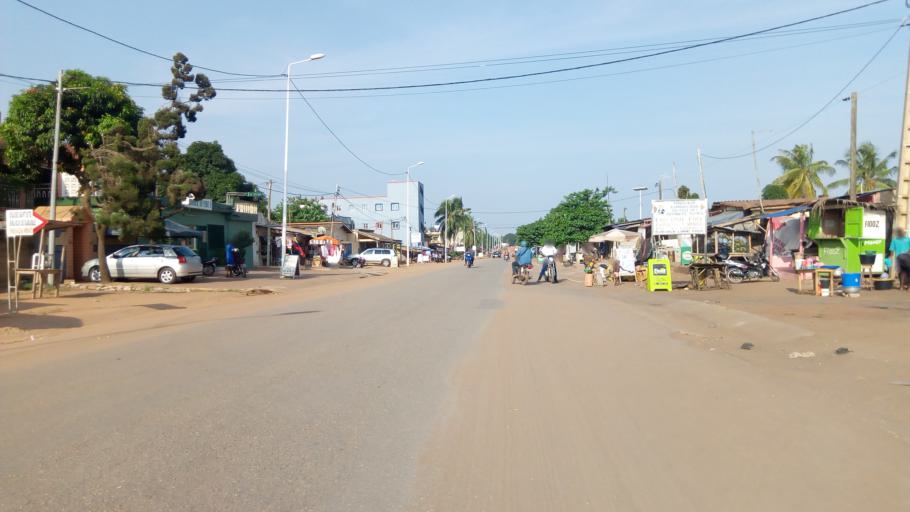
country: TG
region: Maritime
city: Lome
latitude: 6.1812
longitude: 1.1903
